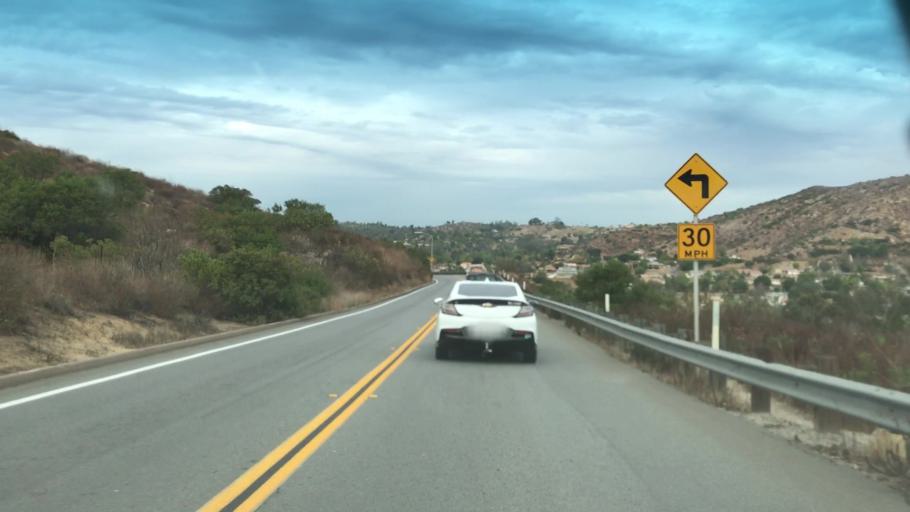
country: US
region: California
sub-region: San Diego County
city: Poway
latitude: 32.9714
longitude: -117.0165
